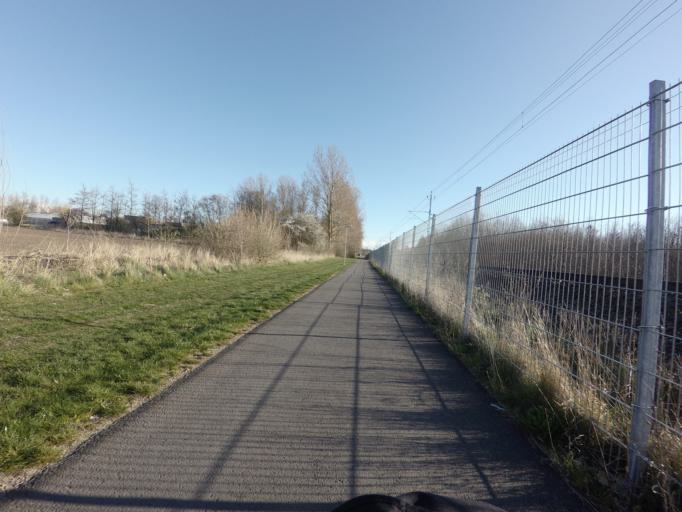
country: SE
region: Skane
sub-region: Lomma Kommun
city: Lomma
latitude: 55.6628
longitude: 13.0748
